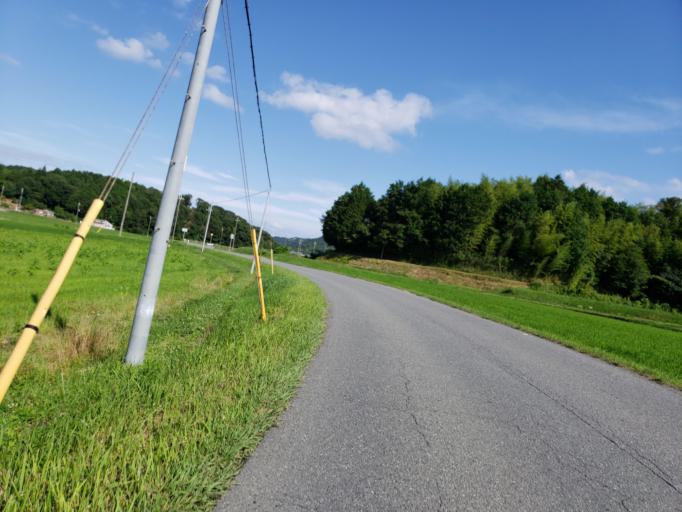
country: JP
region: Hyogo
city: Himeji
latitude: 34.9031
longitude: 134.7942
